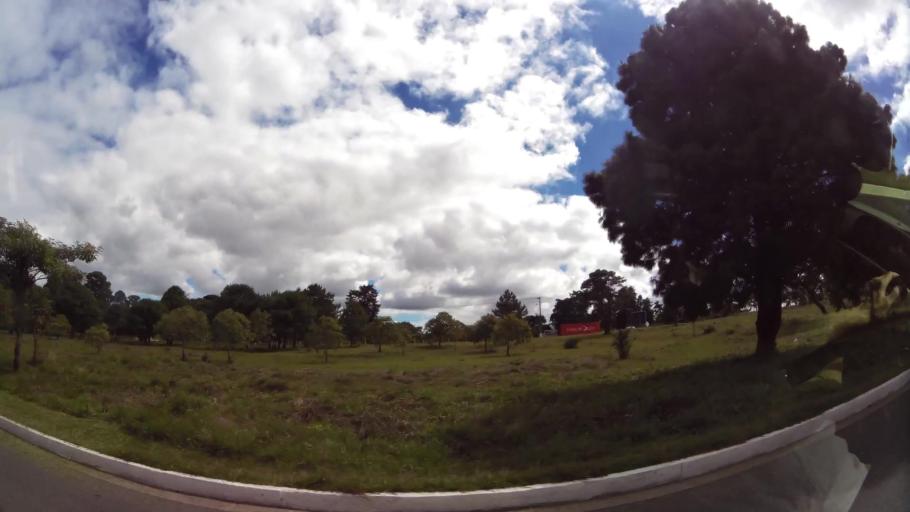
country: GT
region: Guatemala
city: Guatemala City
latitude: 14.6544
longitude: -90.5449
